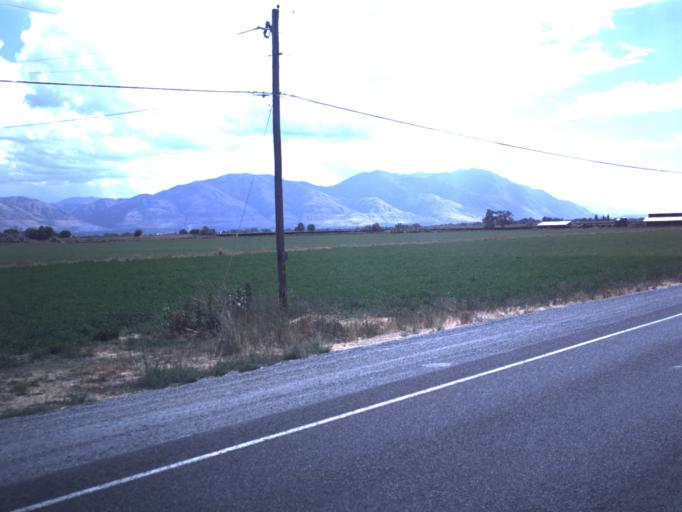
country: US
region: Utah
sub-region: Box Elder County
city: Honeyville
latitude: 41.5835
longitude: -112.1298
